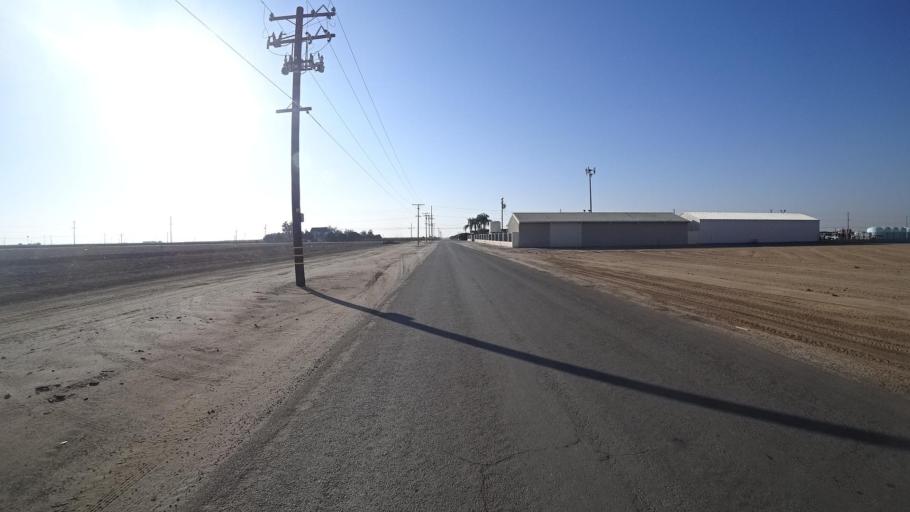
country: US
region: California
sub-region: Tulare County
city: Richgrove
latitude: 35.7776
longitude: -119.1607
